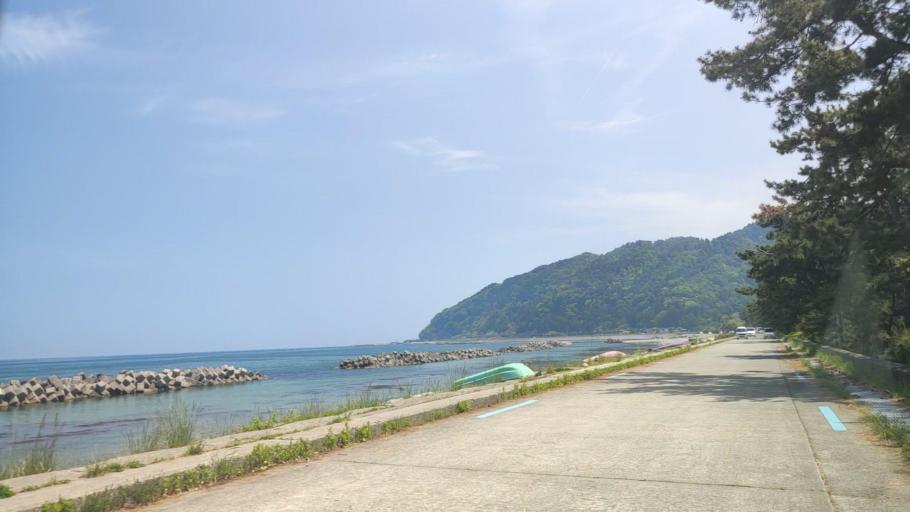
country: JP
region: Toyama
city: Nyuzen
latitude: 36.9629
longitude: 137.5664
